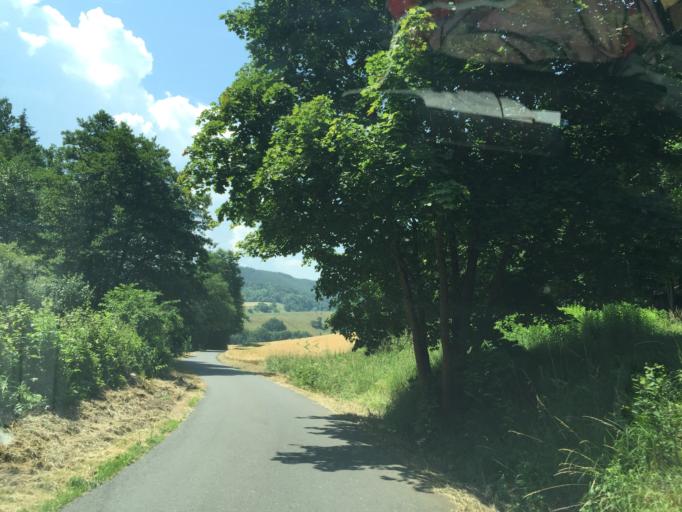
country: DE
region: Thuringia
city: Rudolstadt
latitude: 50.7525
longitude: 11.3186
